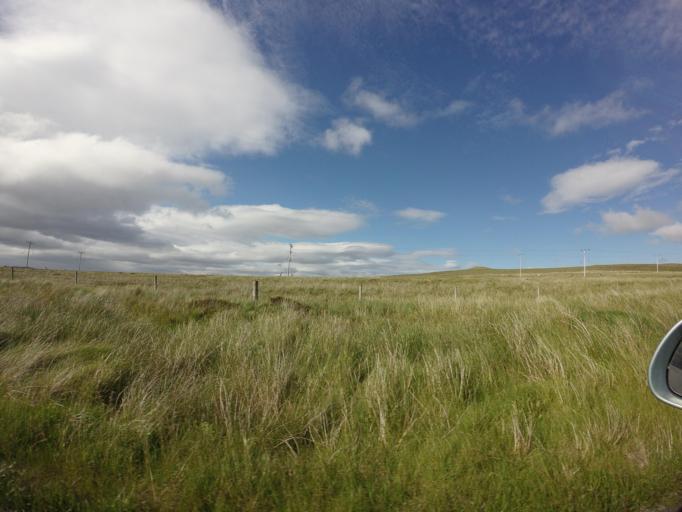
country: GB
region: Scotland
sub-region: Eilean Siar
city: Isle of Lewis
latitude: 58.1772
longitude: -6.6249
